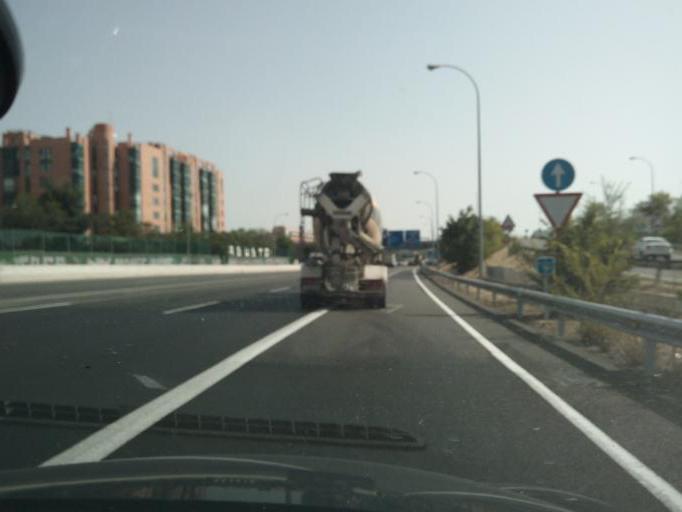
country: ES
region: Madrid
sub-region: Provincia de Madrid
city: Barajas de Madrid
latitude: 40.4539
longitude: -3.5856
